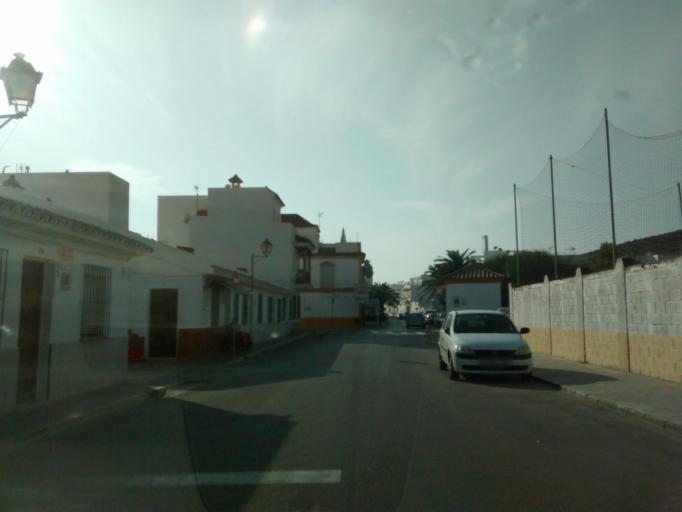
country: ES
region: Andalusia
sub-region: Provincia de Cadiz
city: Zahara de los Atunes
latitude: 36.1361
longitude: -5.8433
